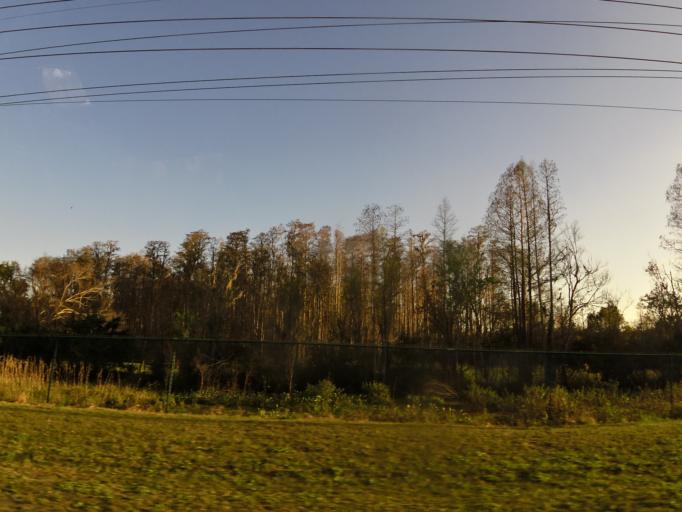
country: US
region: Florida
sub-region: Pasco County
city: Trinity
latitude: 28.1682
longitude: -82.6908
